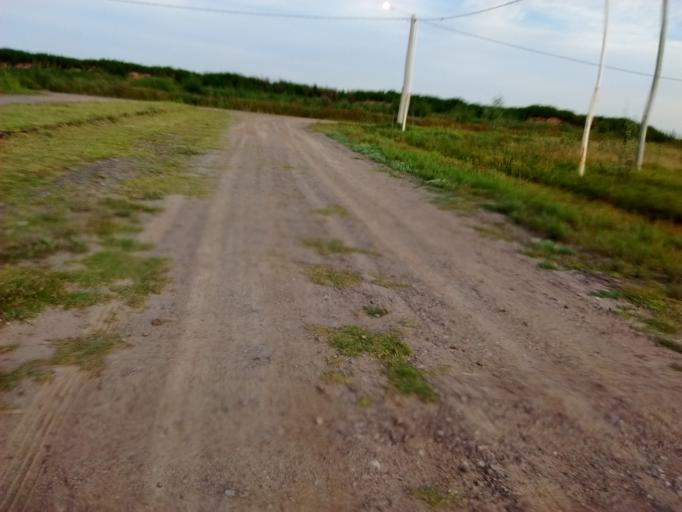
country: AR
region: Santa Fe
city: Roldan
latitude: -32.9389
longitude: -60.8750
